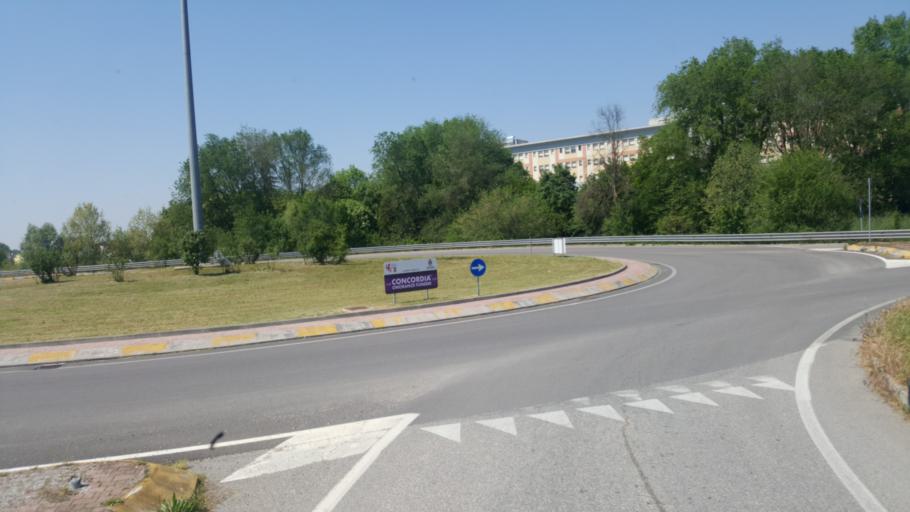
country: IT
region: Lombardy
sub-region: Provincia di Mantova
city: Pieve di Coriano
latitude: 45.0330
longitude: 11.1177
